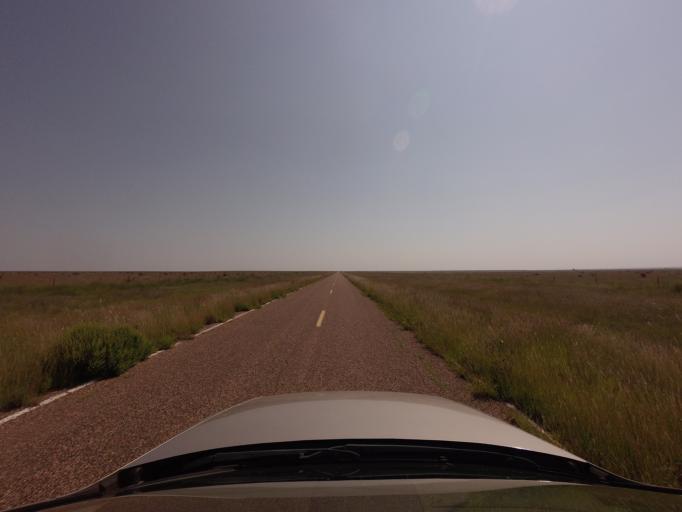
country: US
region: New Mexico
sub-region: Curry County
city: Cannon Air Force Base
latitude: 34.6332
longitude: -103.4218
